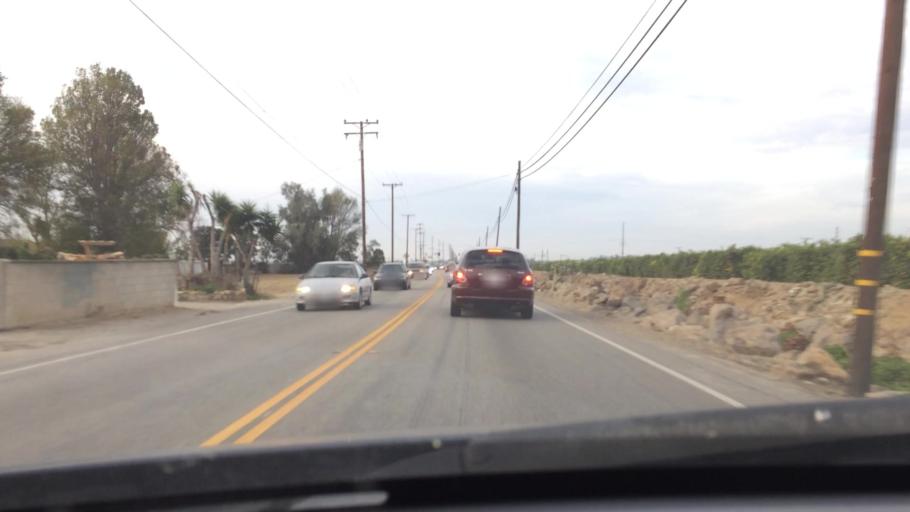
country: US
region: California
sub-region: Ventura County
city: Saticoy
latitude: 34.2585
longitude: -119.1065
